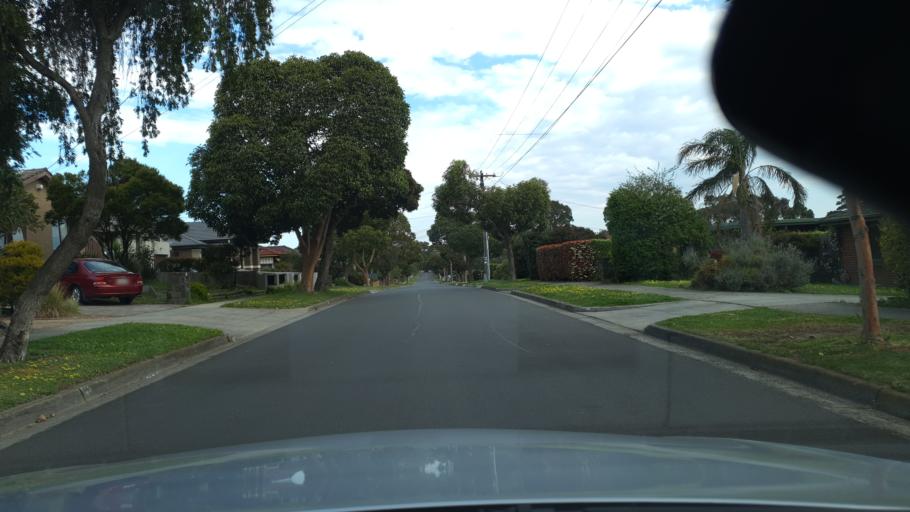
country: AU
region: Victoria
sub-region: Greater Dandenong
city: Noble Park North
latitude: -37.9318
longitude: 145.1792
